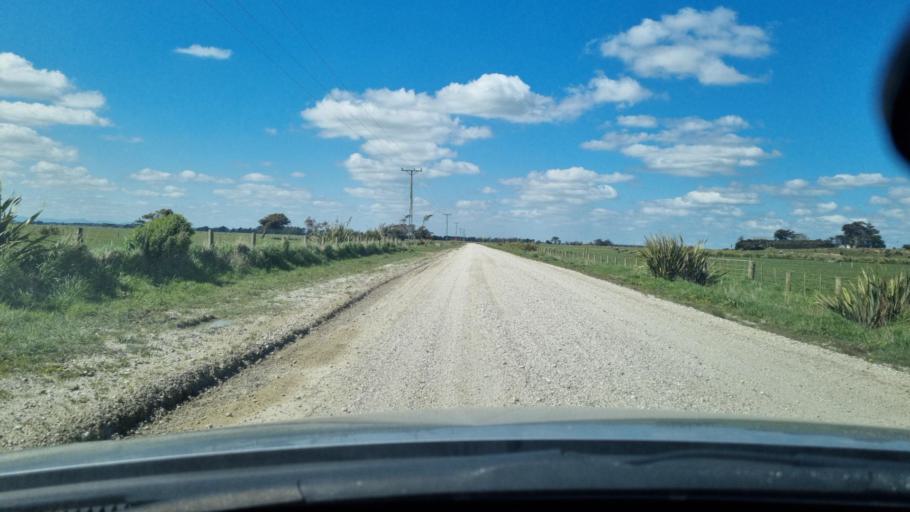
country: NZ
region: Southland
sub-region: Invercargill City
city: Invercargill
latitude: -46.3928
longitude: 168.2486
